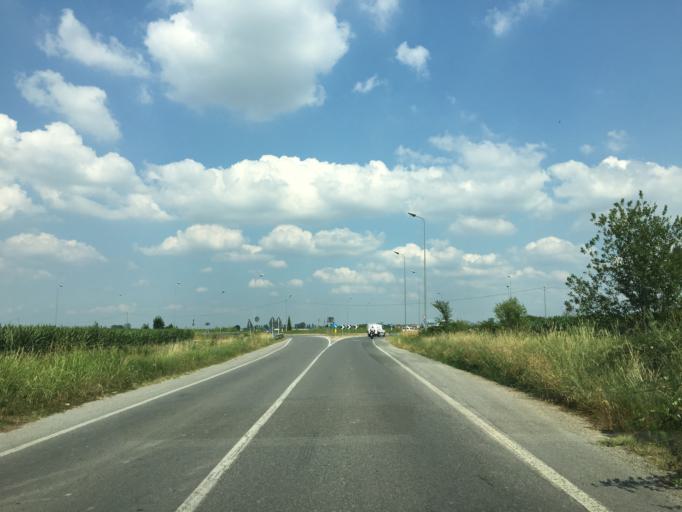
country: IT
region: Piedmont
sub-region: Provincia di Cuneo
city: Racconigi
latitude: 44.7747
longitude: 7.6993
